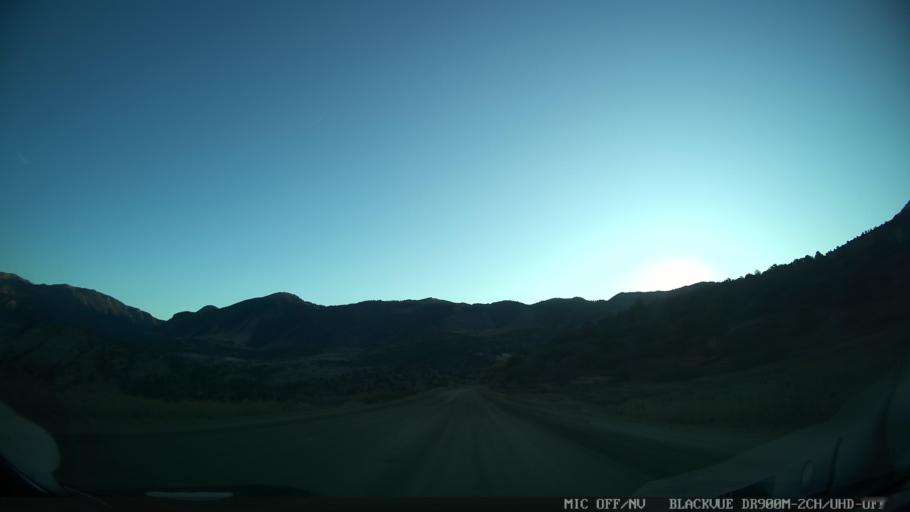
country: US
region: Colorado
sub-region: Grand County
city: Kremmling
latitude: 39.9661
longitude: -106.5122
